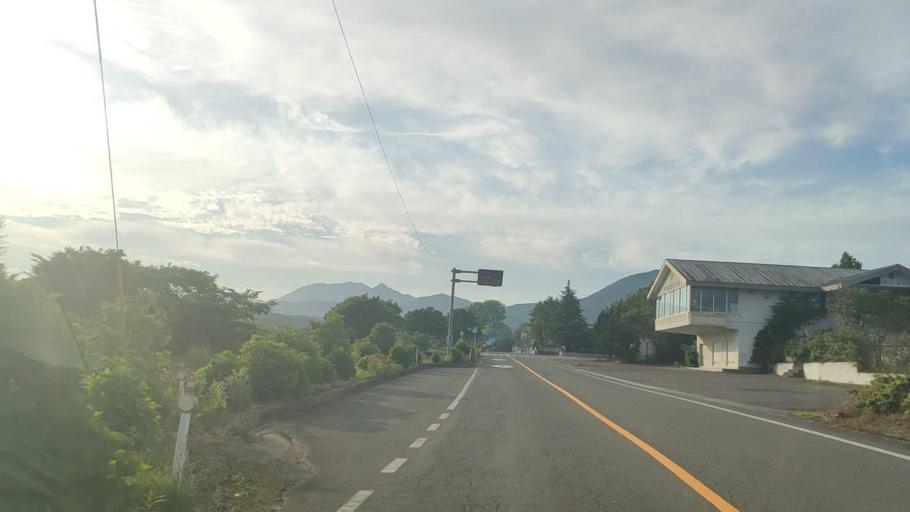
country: JP
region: Tottori
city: Kurayoshi
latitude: 35.2959
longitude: 133.6342
